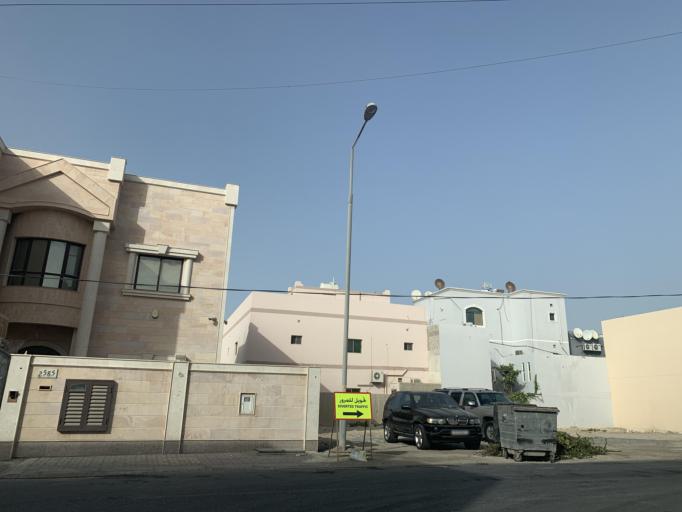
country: BH
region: Central Governorate
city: Madinat Hamad
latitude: 26.1555
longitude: 50.5095
